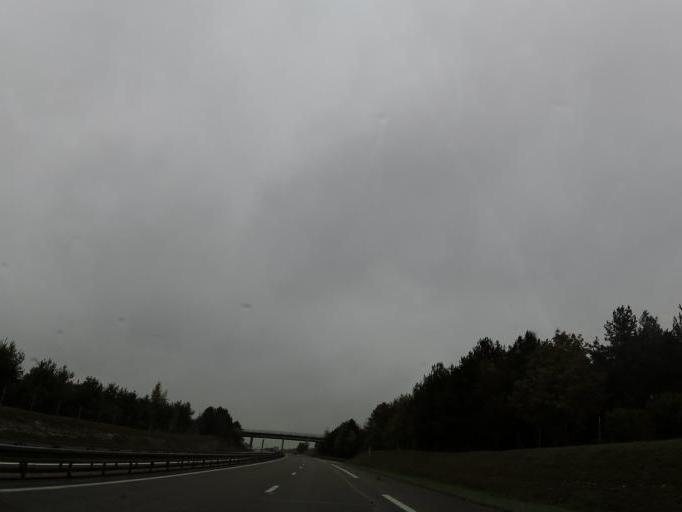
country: FR
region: Champagne-Ardenne
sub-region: Departement de la Marne
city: Fagnieres
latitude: 49.0399
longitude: 4.3437
